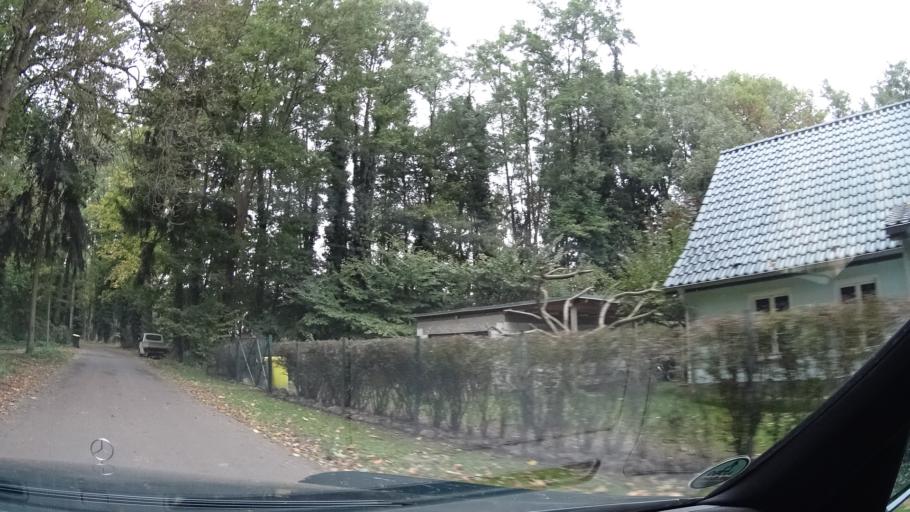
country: DE
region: Brandenburg
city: Neuruppin
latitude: 52.9370
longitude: 12.8209
